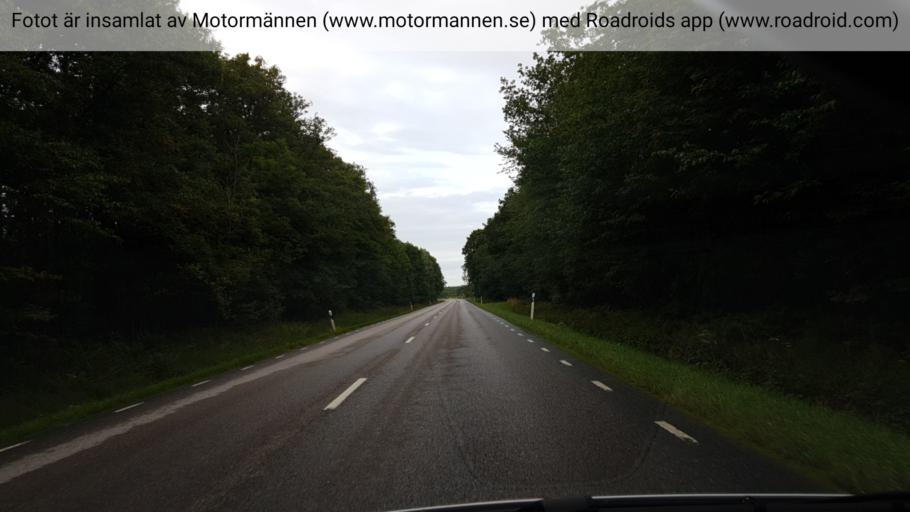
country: SE
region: Vaestra Goetaland
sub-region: Hjo Kommun
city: Hjo
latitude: 58.2347
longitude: 14.2211
